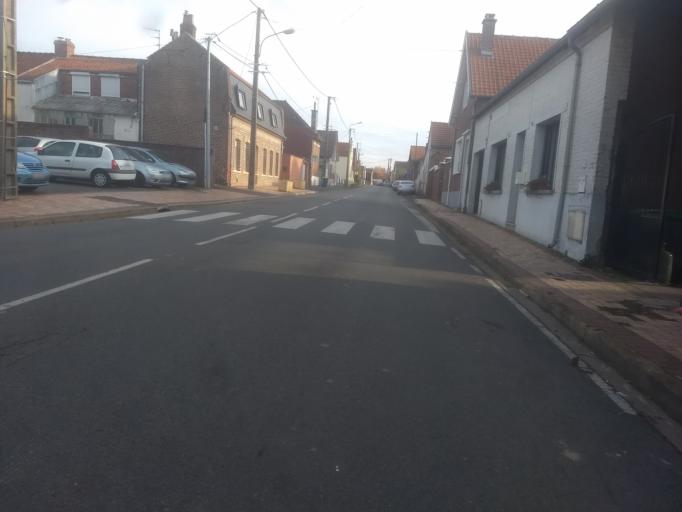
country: FR
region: Nord-Pas-de-Calais
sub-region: Departement du Pas-de-Calais
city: Agny
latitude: 50.2601
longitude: 2.7602
